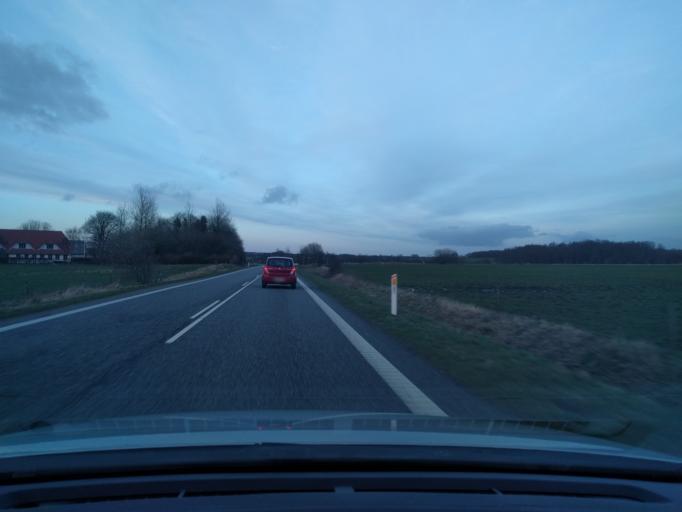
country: DK
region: South Denmark
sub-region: Tonder Kommune
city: Toftlund
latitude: 55.1567
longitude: 9.0372
